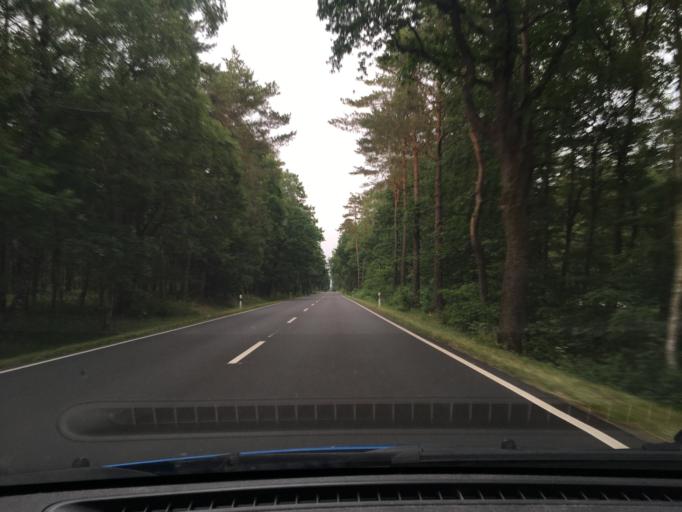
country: DE
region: Lower Saxony
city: Bispingen
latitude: 53.0676
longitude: 10.0513
